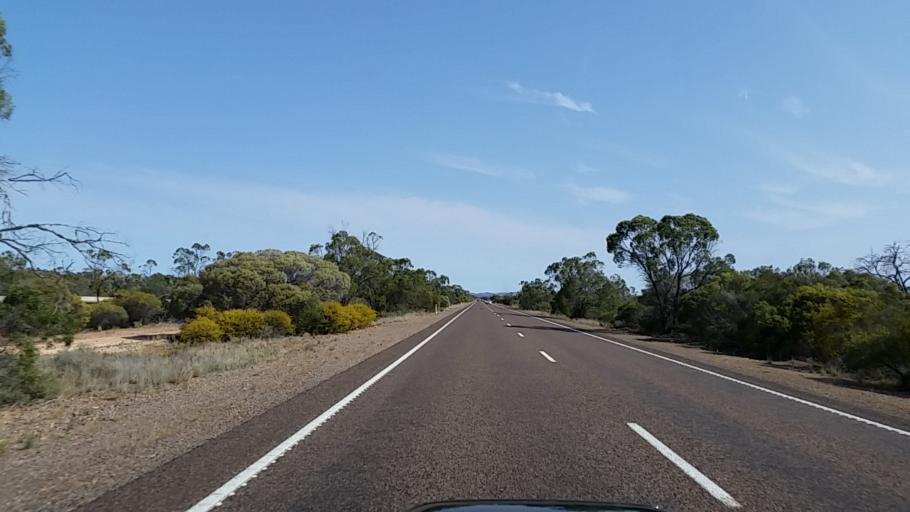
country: AU
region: South Australia
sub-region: Port Augusta
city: Port Augusta West
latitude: -32.6625
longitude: 137.5302
